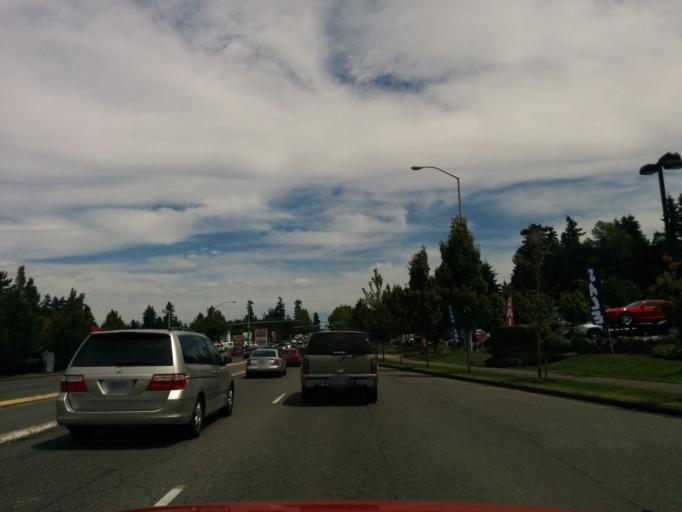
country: US
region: Washington
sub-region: King County
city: Kirkland
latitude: 47.6792
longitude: -122.1824
